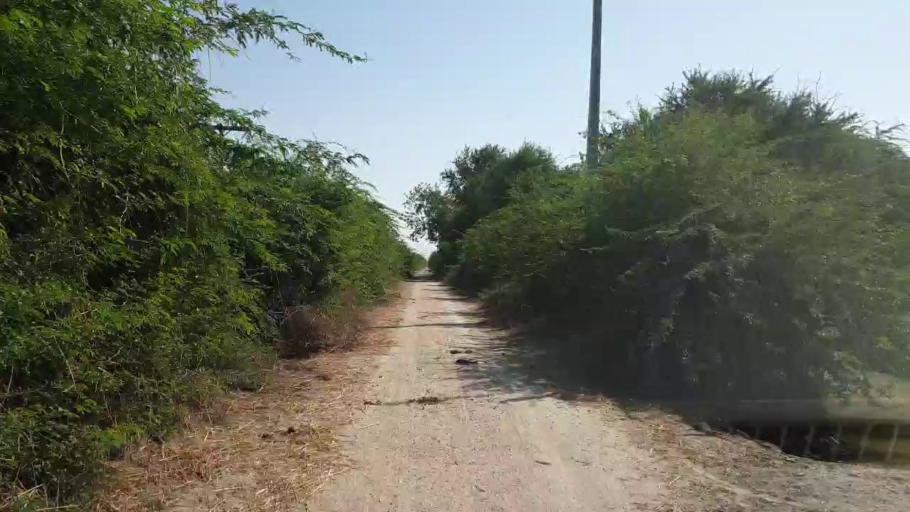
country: PK
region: Sindh
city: Tando Bago
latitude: 24.6408
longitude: 68.9893
